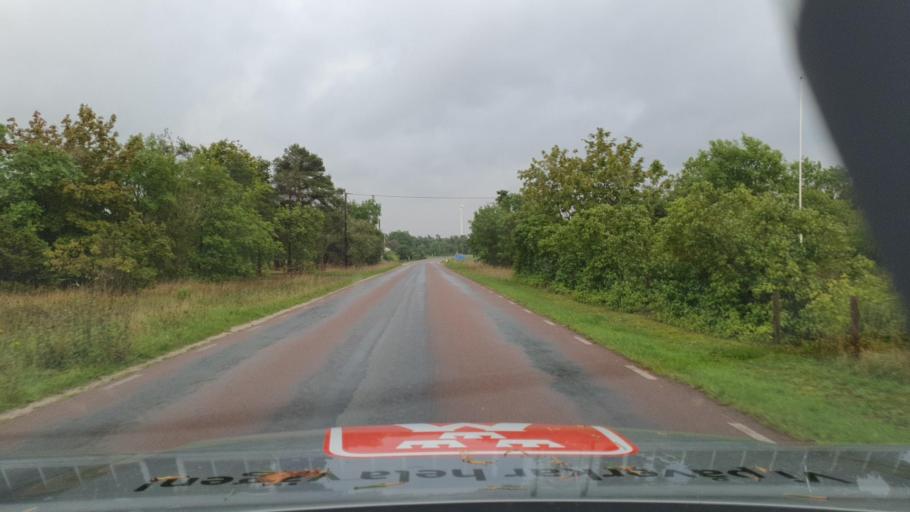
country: SE
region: Gotland
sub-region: Gotland
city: Visby
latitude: 57.6527
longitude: 18.5463
